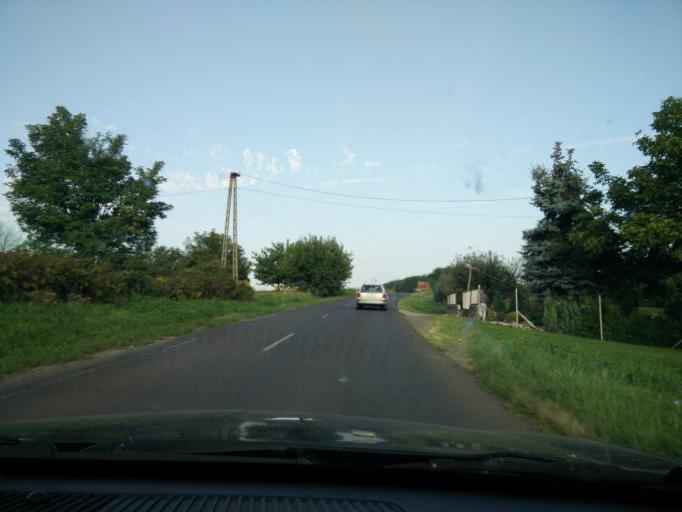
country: HU
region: Tolna
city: Nagymanyok
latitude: 46.2789
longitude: 18.4504
